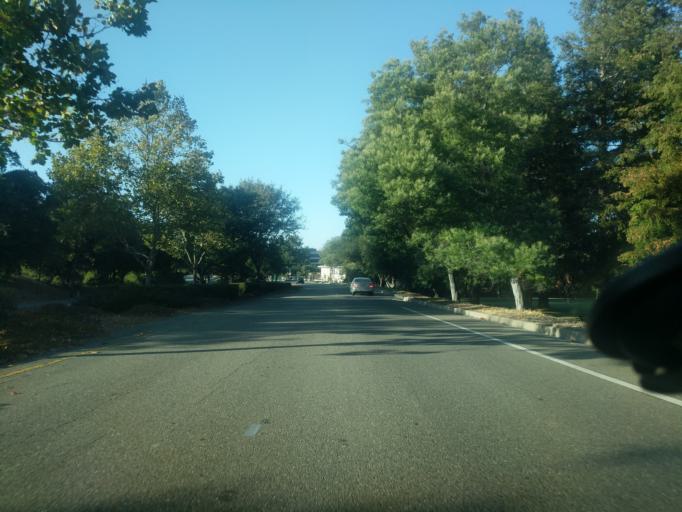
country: US
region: California
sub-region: Alameda County
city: Dublin
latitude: 37.6865
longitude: -121.9297
